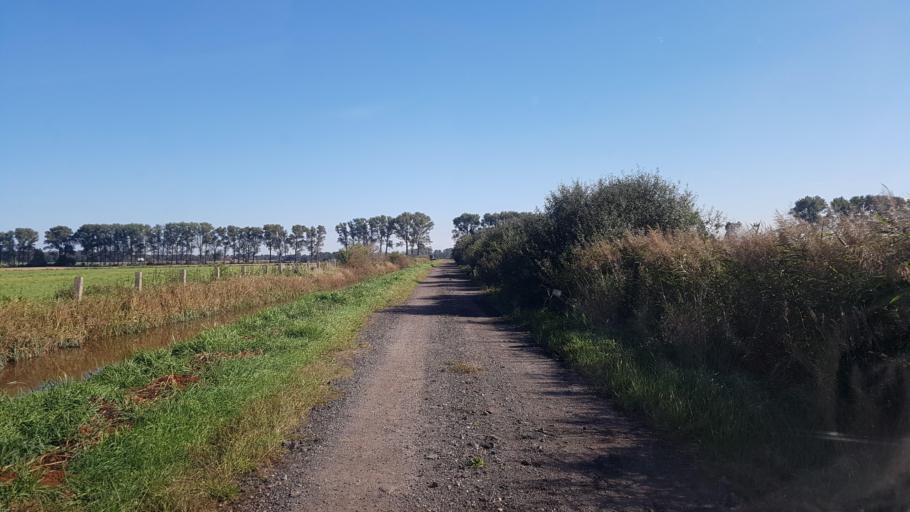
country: DE
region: Brandenburg
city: Plessa
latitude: 51.4598
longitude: 13.5795
